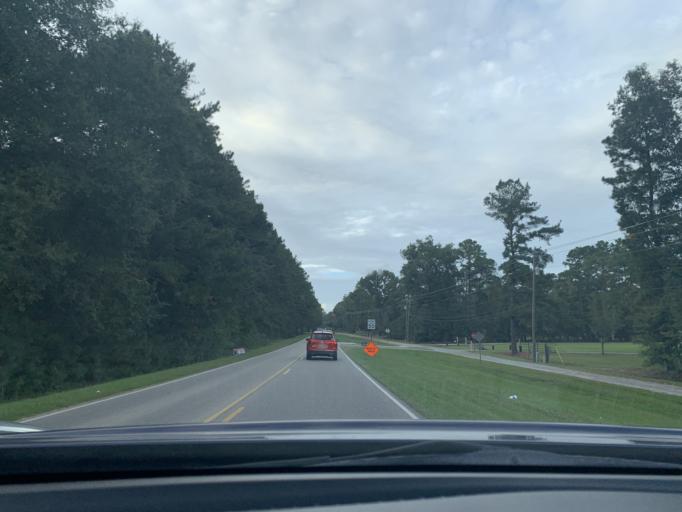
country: US
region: Georgia
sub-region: Chatham County
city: Georgetown
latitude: 32.0445
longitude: -81.2628
